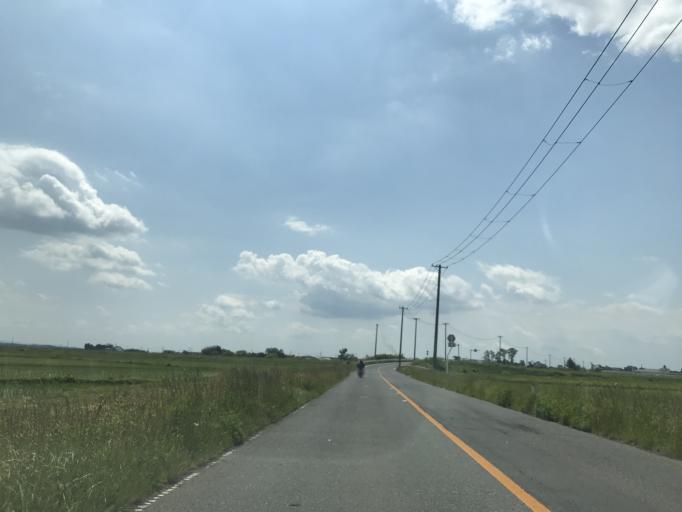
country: JP
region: Miyagi
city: Kogota
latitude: 38.5910
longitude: 141.0301
